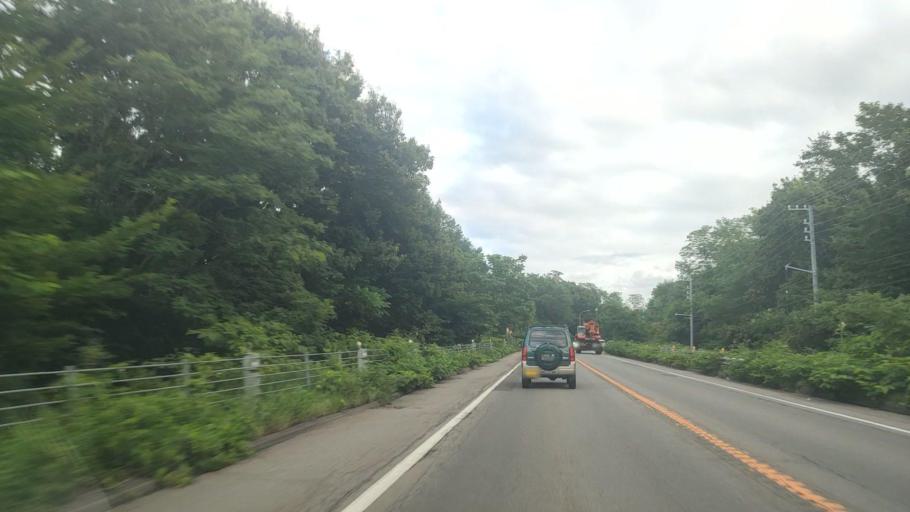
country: JP
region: Hokkaido
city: Nanae
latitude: 42.0733
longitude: 140.6019
